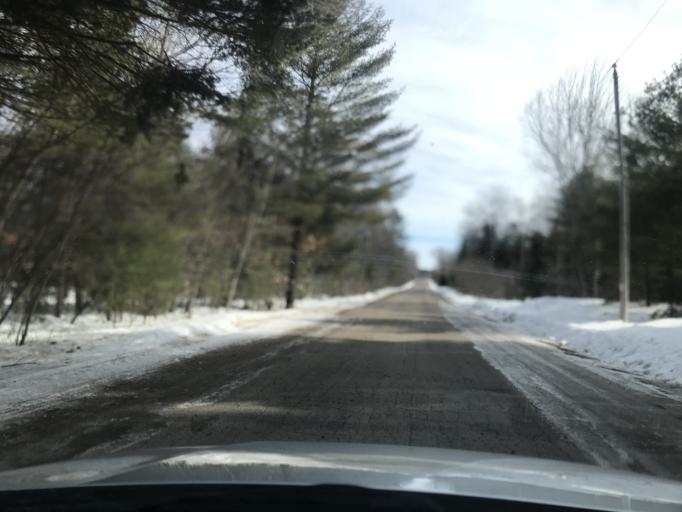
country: US
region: Wisconsin
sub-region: Menominee County
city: Legend Lake
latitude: 45.1054
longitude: -88.4322
